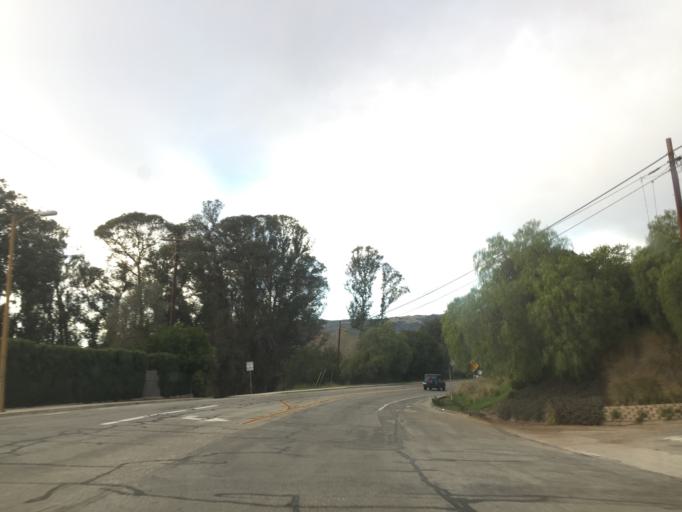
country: US
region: California
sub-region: Santa Barbara County
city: Goleta
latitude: 34.4477
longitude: -119.7914
